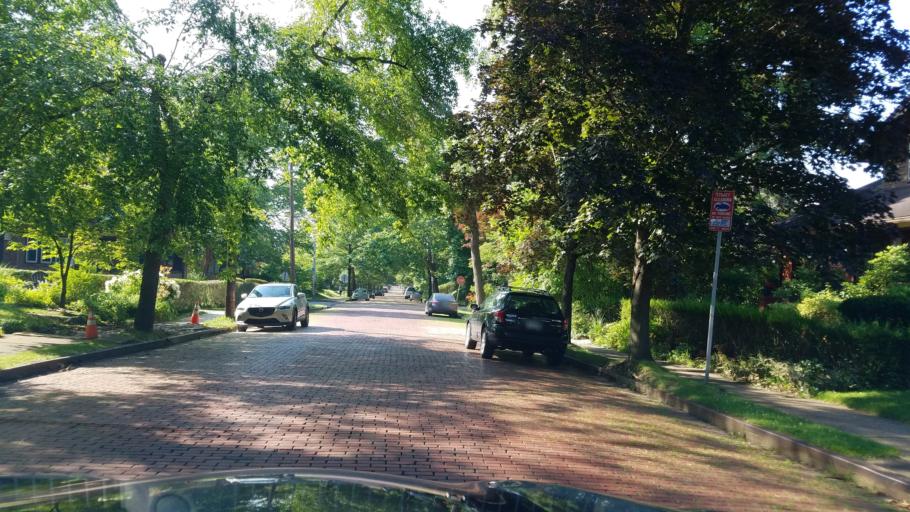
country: US
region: Pennsylvania
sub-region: Allegheny County
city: Edgewood
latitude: 40.4327
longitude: -79.8965
